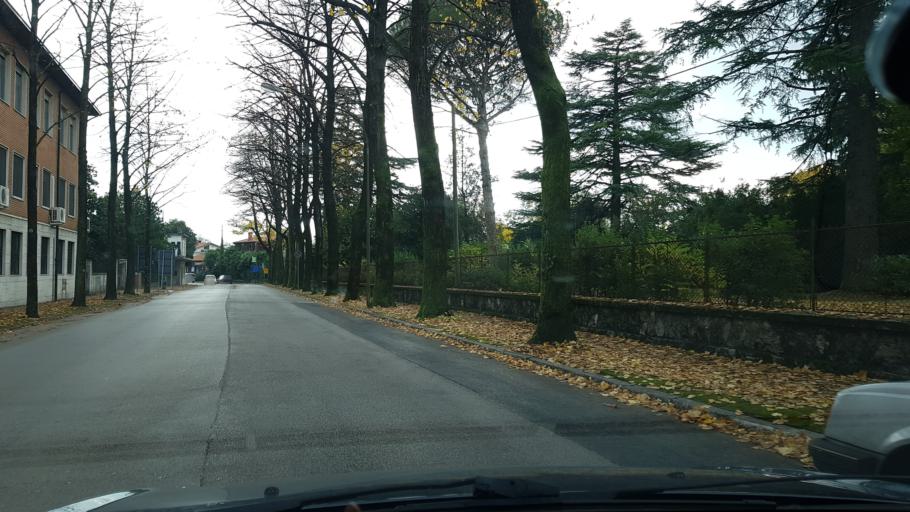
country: SI
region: Sempeter-Vrtojba
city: Sempeter pri Gorici
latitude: 45.9338
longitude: 13.6336
